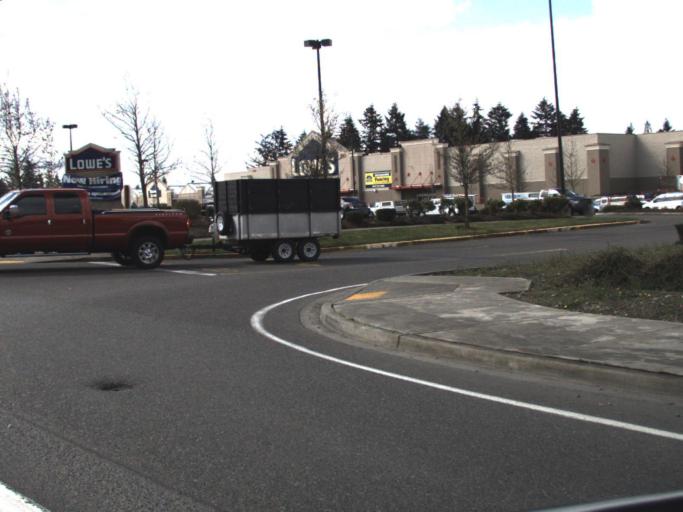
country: US
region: Washington
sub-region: King County
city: Lakeland South
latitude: 47.2850
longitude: -122.3136
